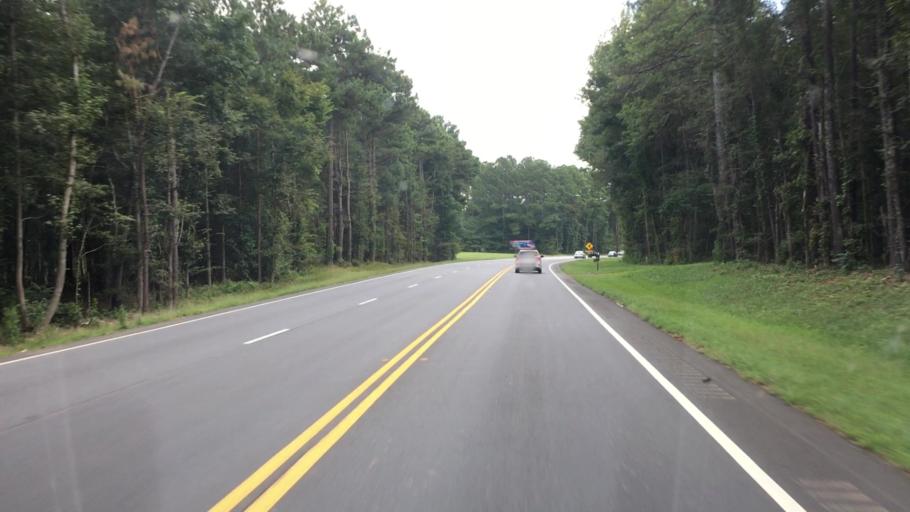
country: US
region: Georgia
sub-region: Putnam County
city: Jefferson
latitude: 33.4361
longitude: -83.3799
